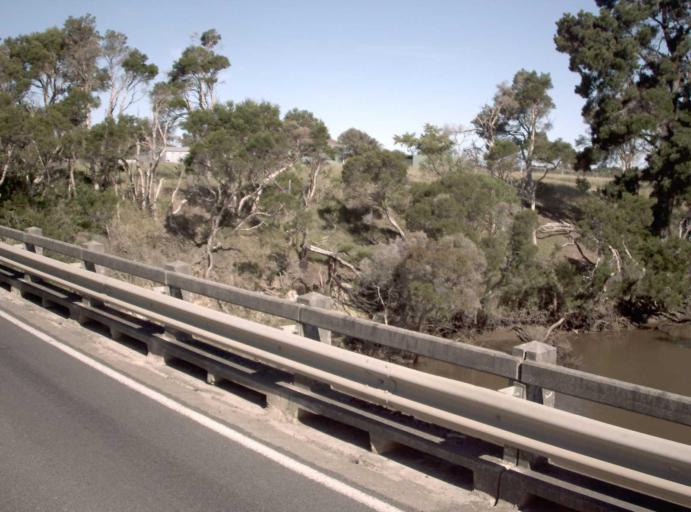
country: AU
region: Victoria
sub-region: Latrobe
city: Traralgon
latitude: -38.6222
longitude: 146.6645
